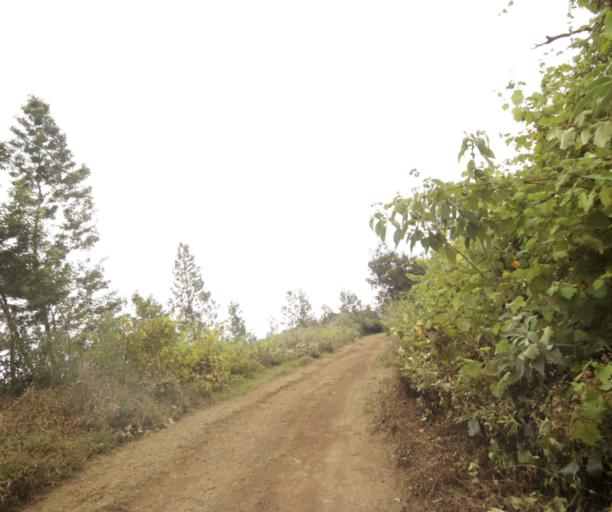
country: RE
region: Reunion
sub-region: Reunion
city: La Possession
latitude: -21.0122
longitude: 55.3602
